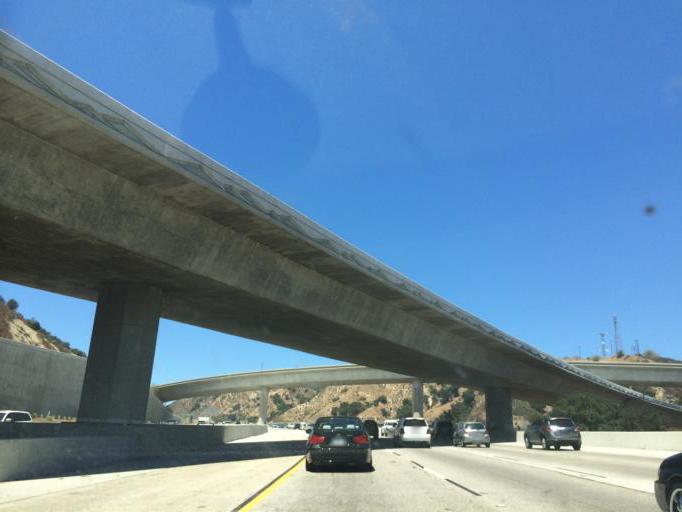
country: US
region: California
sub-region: Los Angeles County
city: Santa Clarita
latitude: 34.3337
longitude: -118.5081
